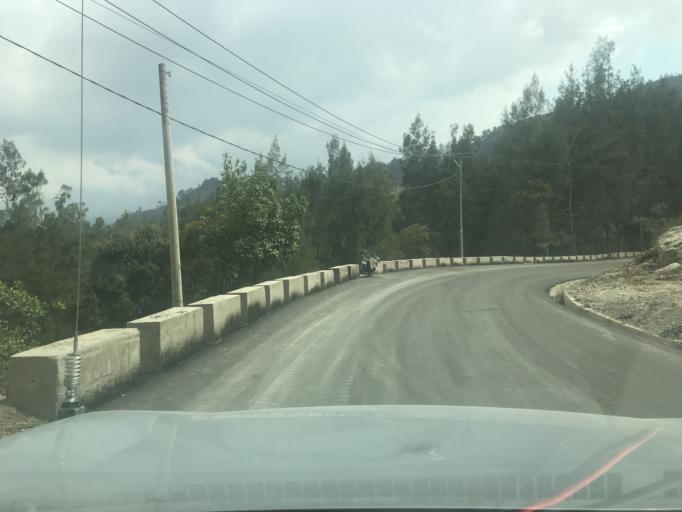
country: TL
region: Manufahi
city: Same
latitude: -8.8948
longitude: 125.5929
